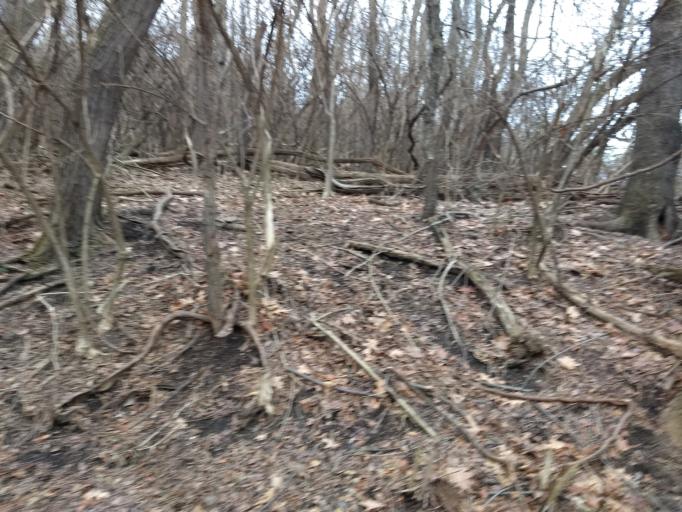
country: US
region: Pennsylvania
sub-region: Allegheny County
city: Homestead
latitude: 40.4061
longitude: -79.9352
